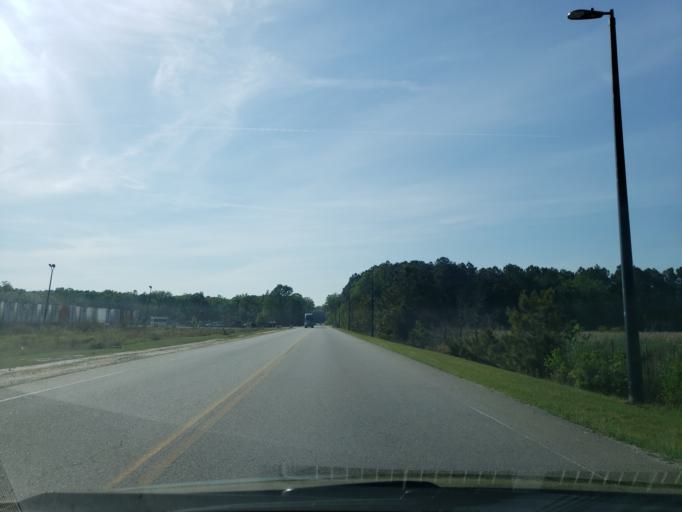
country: US
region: Georgia
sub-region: Chatham County
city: Garden City
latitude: 32.1024
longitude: -81.1880
